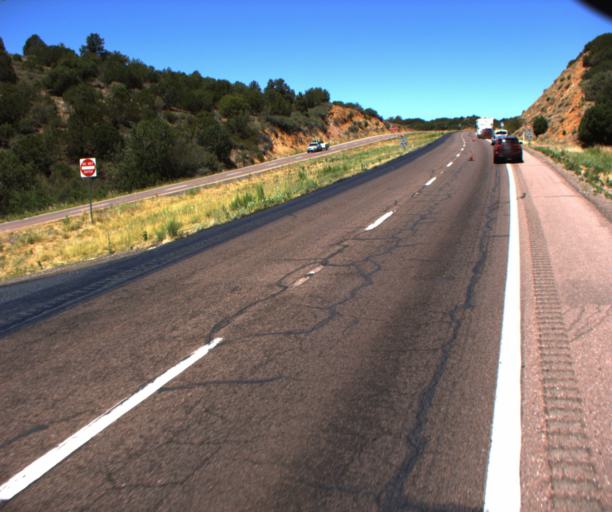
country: US
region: Arizona
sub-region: Gila County
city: Payson
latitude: 34.1640
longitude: -111.3277
